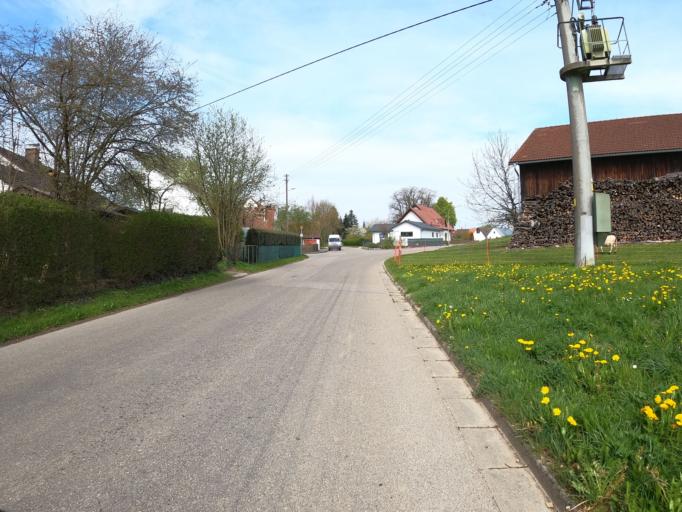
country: DE
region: Bavaria
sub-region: Swabia
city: Pfaffenhofen an der Roth
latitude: 48.3944
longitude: 10.1994
